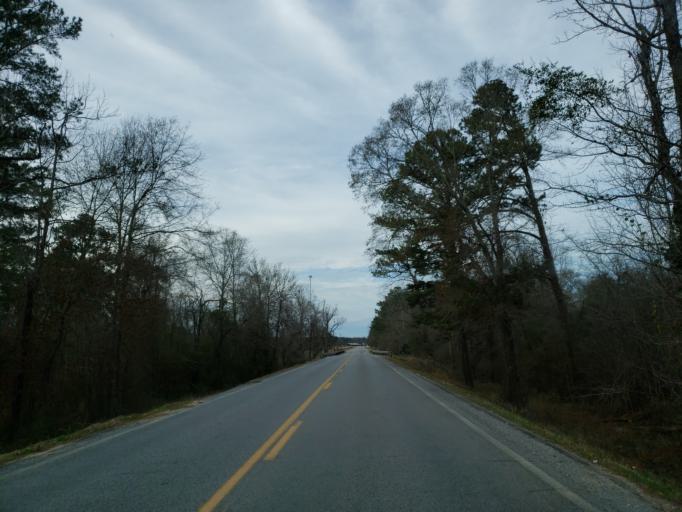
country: US
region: Mississippi
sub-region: Clarke County
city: Quitman
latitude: 31.8743
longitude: -88.7063
